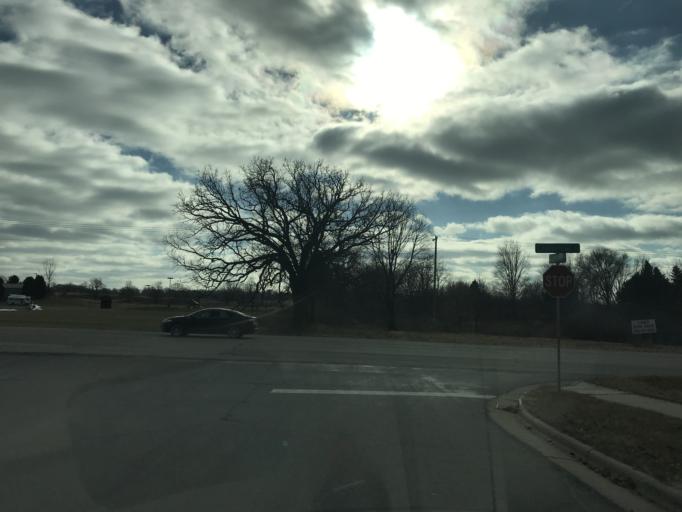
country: US
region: Wisconsin
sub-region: Dane County
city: Monona
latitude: 43.1068
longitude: -89.2913
